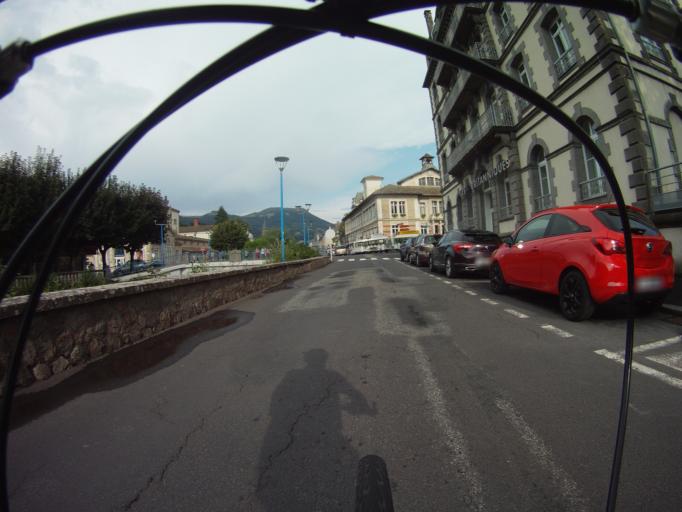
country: FR
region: Auvergne
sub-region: Departement du Puy-de-Dome
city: La Bourboule
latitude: 45.5876
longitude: 2.7377
